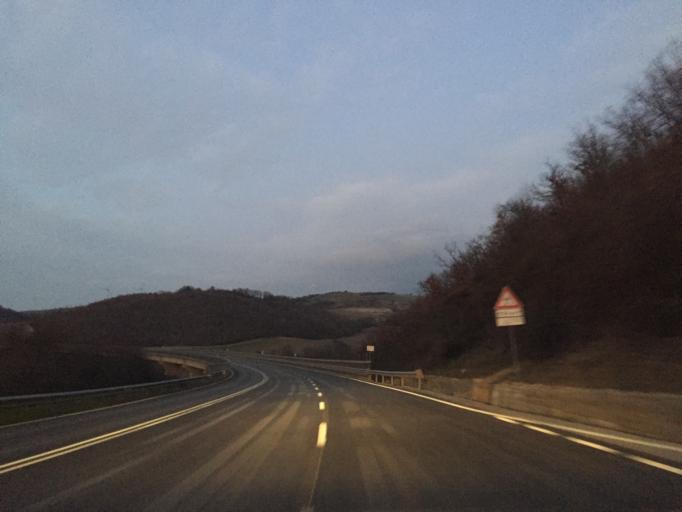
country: IT
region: Apulia
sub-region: Provincia di Foggia
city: Volturino
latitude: 41.4587
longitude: 15.0909
